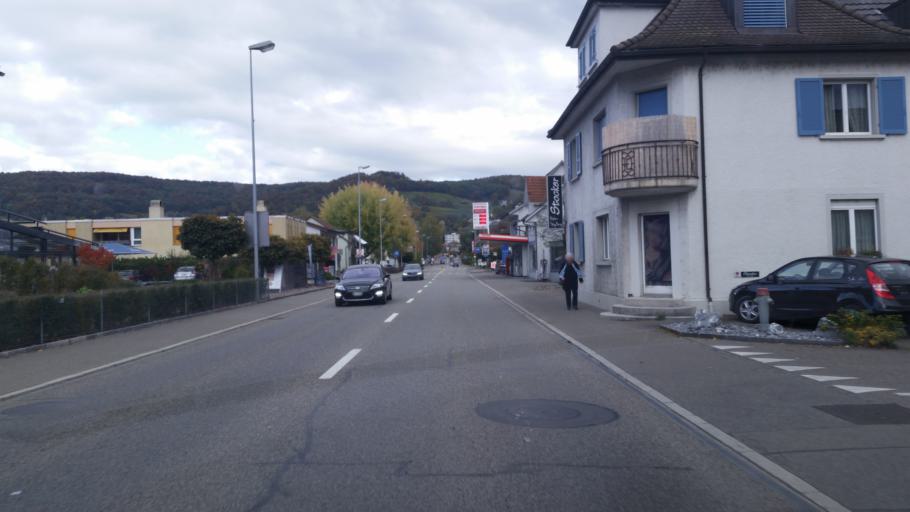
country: CH
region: Aargau
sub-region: Bezirk Zurzach
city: Klingnau
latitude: 47.5711
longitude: 8.2476
